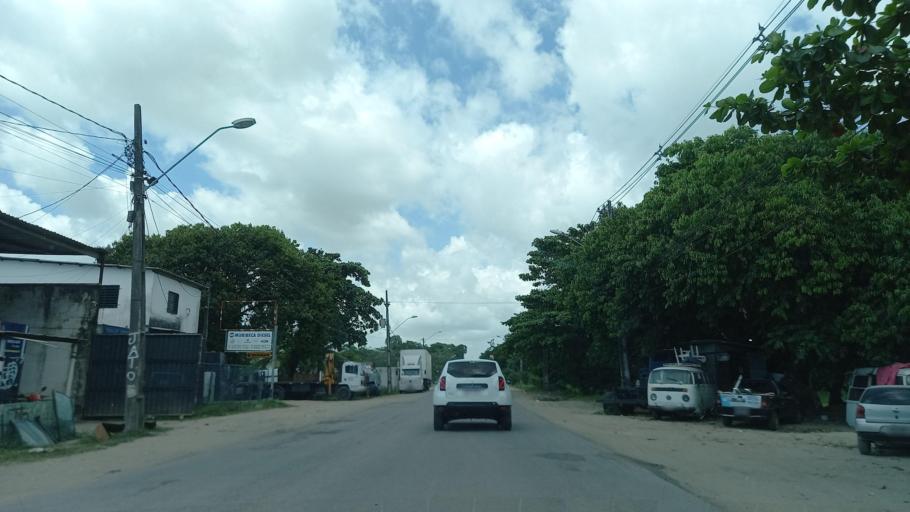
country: BR
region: Pernambuco
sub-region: Jaboatao Dos Guararapes
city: Jaboatao
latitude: -8.1580
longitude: -34.9734
